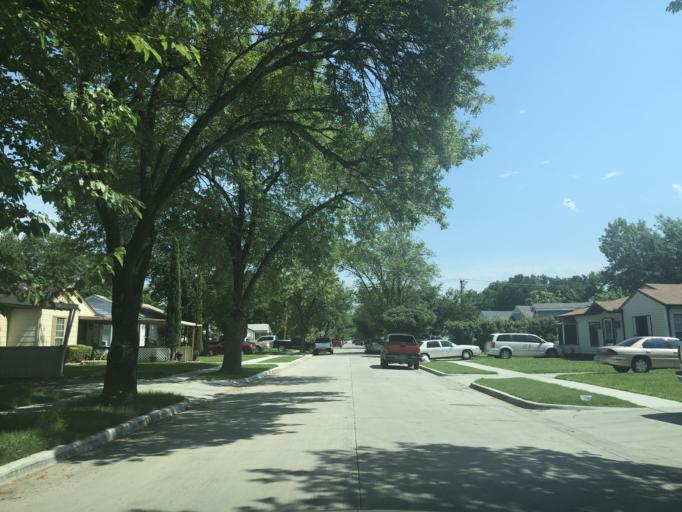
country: US
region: Texas
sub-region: Dallas County
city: Grand Prairie
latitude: 32.7323
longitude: -97.0081
